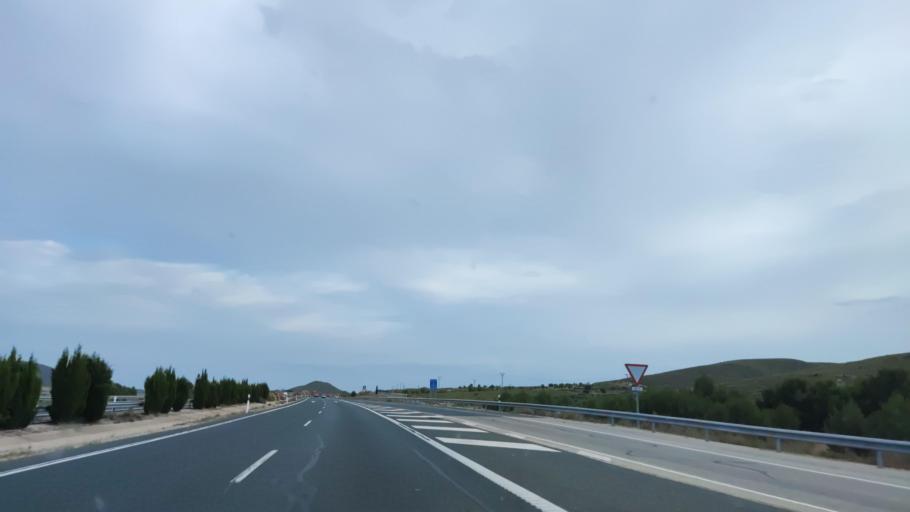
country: ES
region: Castille-La Mancha
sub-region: Provincia de Albacete
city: Tobarra
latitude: 38.5731
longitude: -1.6877
